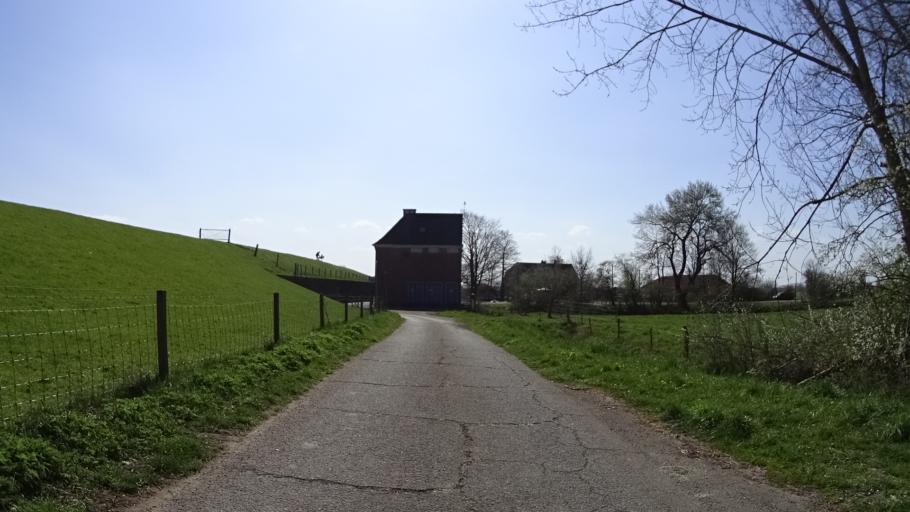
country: DE
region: Lower Saxony
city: Weener
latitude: 53.1341
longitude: 7.3628
